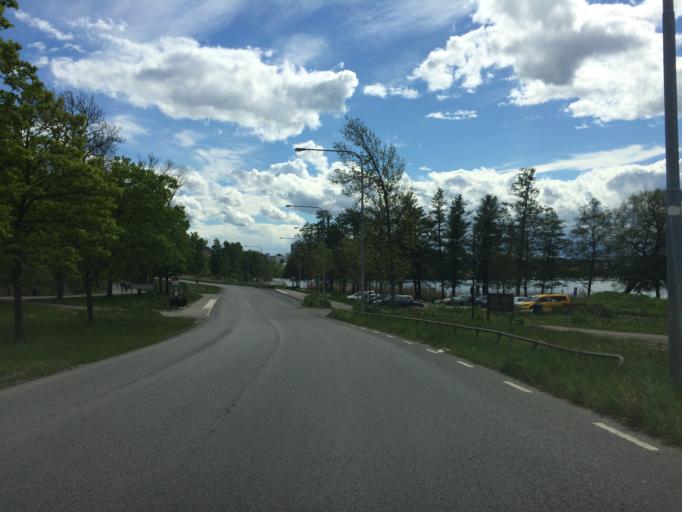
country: SE
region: Stockholm
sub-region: Botkyrka Kommun
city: Fittja
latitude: 59.2625
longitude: 17.8787
